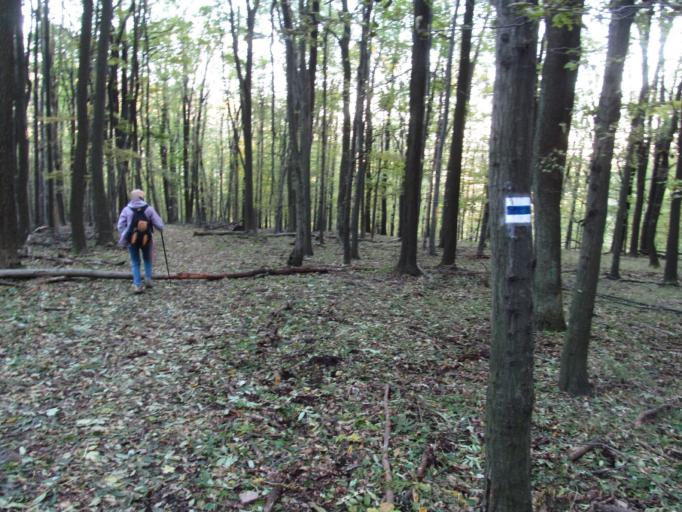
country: HU
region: Heves
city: Paradsasvar
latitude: 47.8929
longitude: 19.9708
